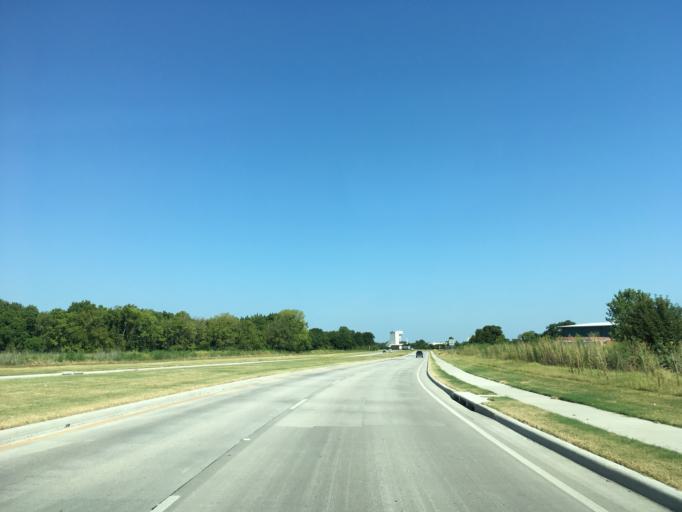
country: US
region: Texas
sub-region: Collin County
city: Fairview
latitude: 33.1668
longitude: -96.6016
